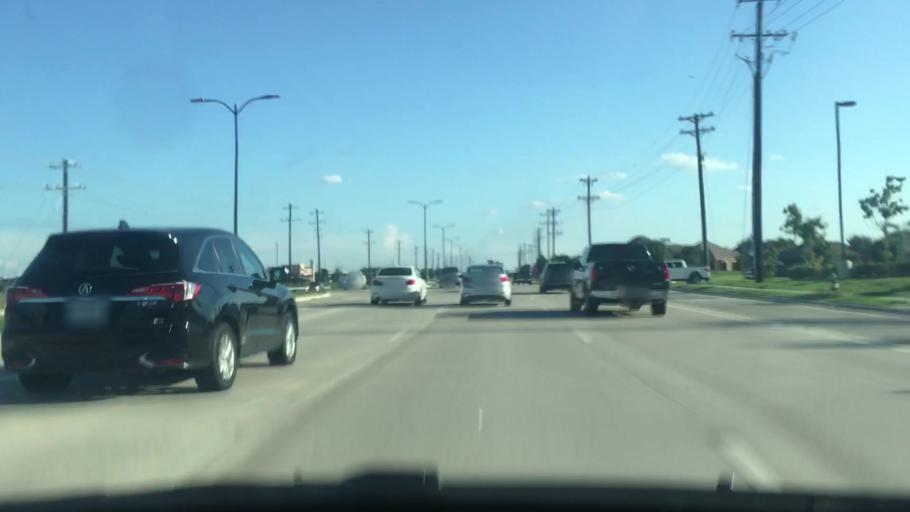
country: US
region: Texas
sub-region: Denton County
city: Little Elm
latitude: 33.1850
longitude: -96.8872
